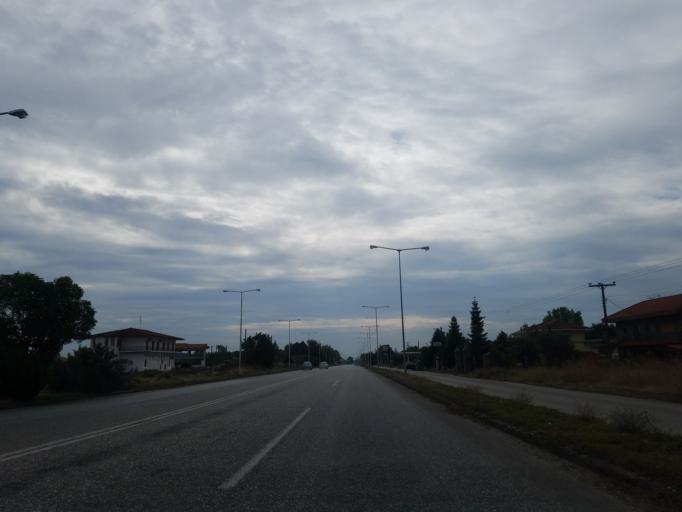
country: GR
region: Thessaly
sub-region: Trikala
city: Pyrgetos
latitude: 39.5823
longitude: 21.7407
